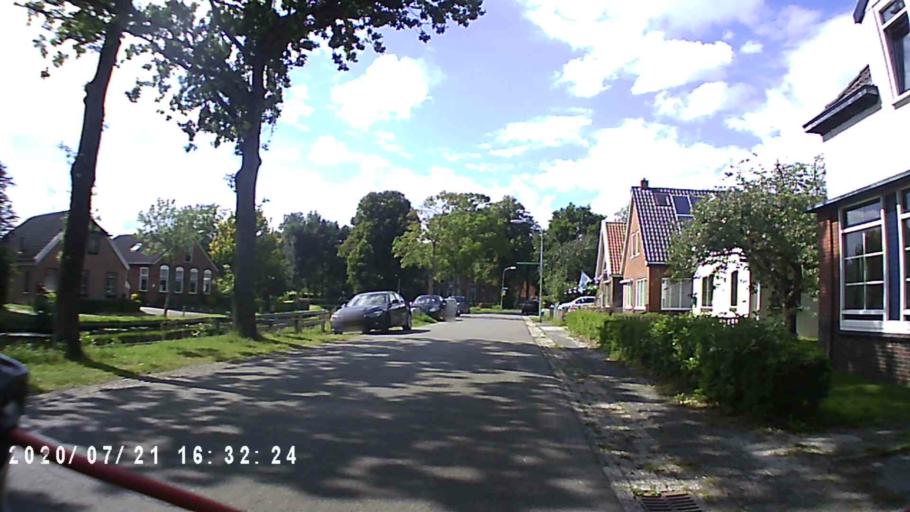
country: NL
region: Groningen
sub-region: Gemeente Hoogezand-Sappemeer
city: Sappemeer
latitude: 53.0845
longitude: 6.7912
